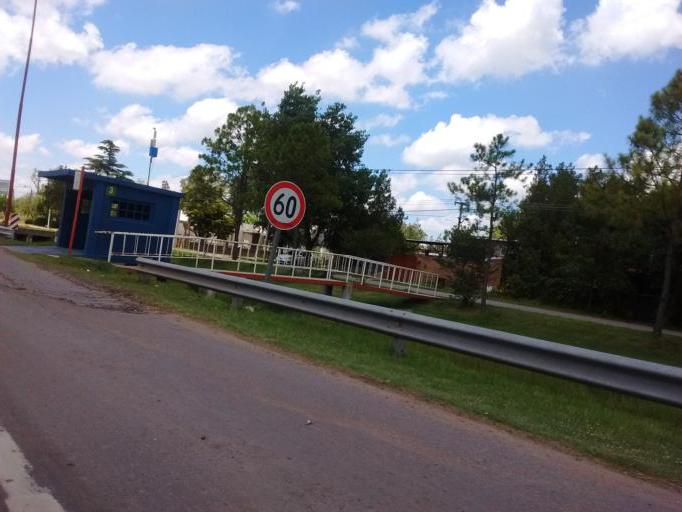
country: AR
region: Santa Fe
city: Funes
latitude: -32.9240
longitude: -60.7834
